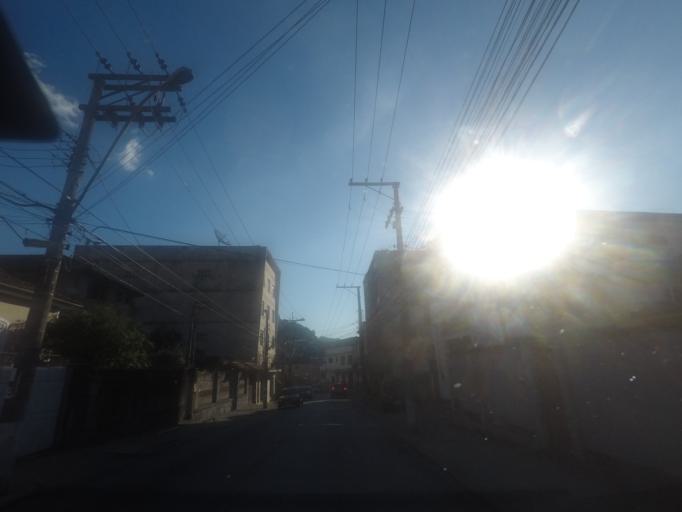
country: BR
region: Rio de Janeiro
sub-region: Petropolis
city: Petropolis
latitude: -22.4877
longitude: -43.1520
